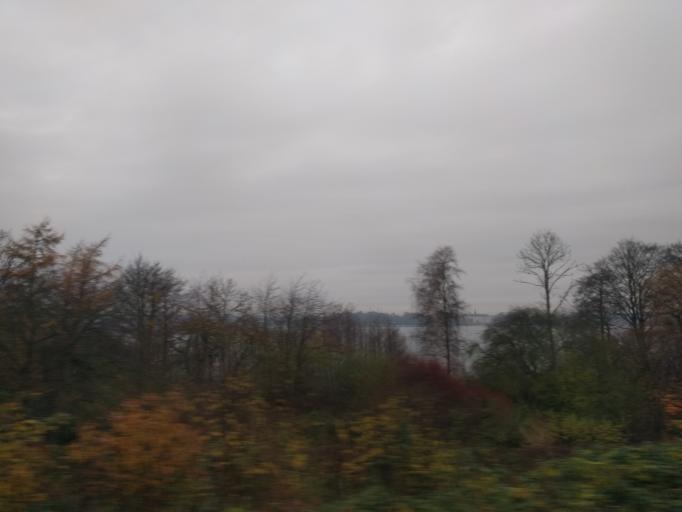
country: DK
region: Zealand
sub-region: Soro Kommune
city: Soro
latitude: 55.4183
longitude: 11.5485
